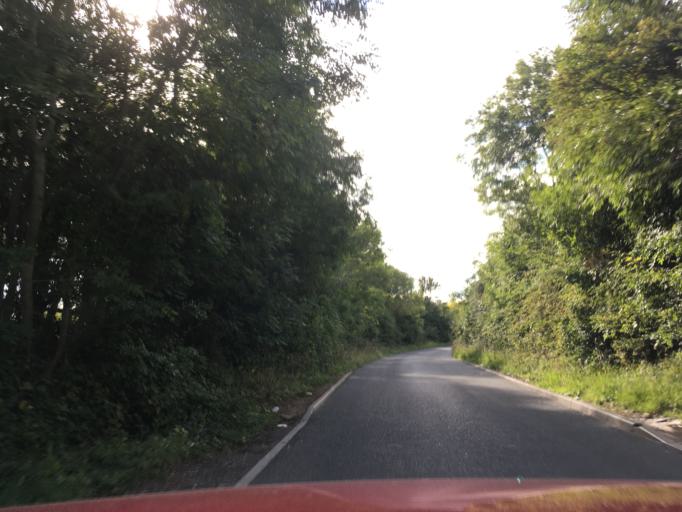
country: GB
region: England
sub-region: Gloucestershire
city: Gloucester
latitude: 51.8096
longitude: -2.2626
